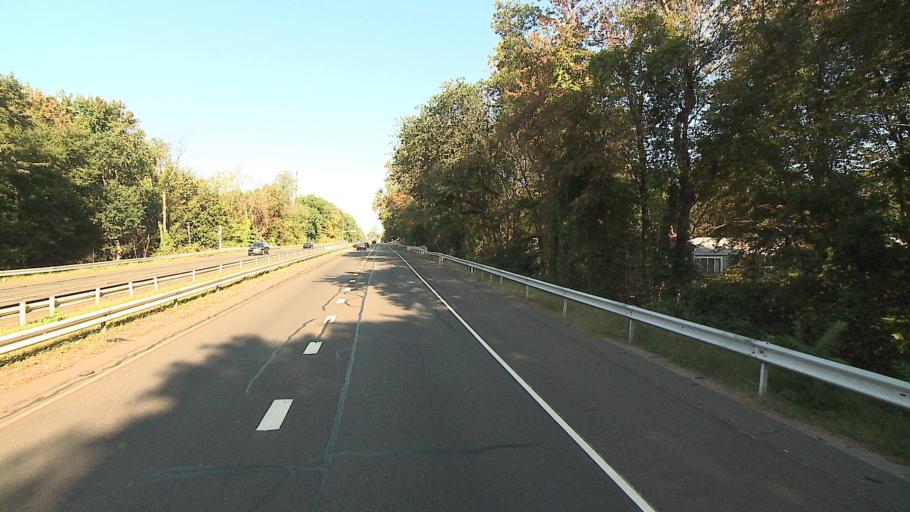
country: US
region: Connecticut
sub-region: New Haven County
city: City of Milford (balance)
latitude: 41.2399
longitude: -73.0777
